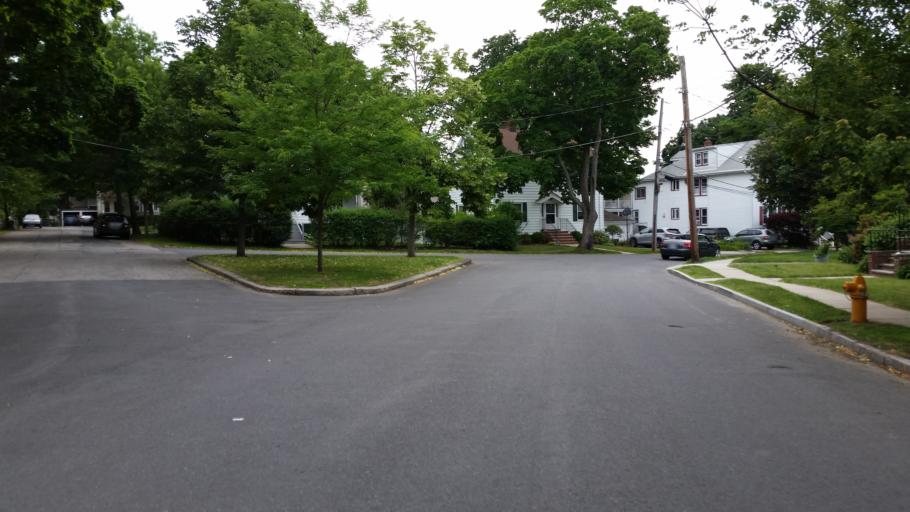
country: US
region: Massachusetts
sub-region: Middlesex County
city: Belmont
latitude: 42.3898
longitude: -71.1779
